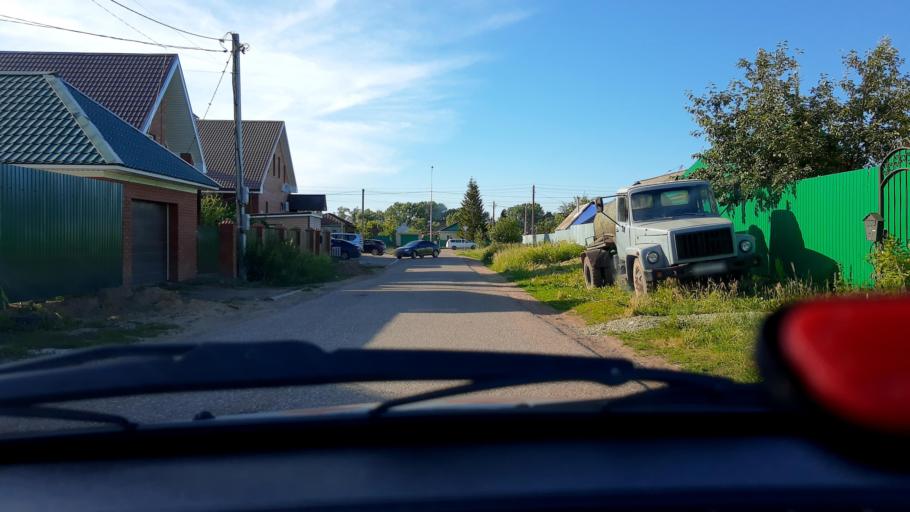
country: RU
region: Bashkortostan
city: Avdon
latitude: 54.4996
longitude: 55.8968
